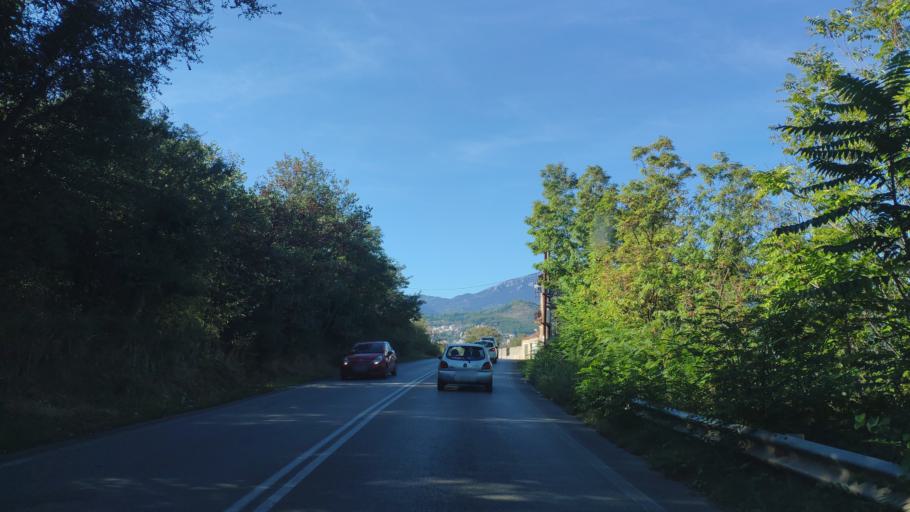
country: GR
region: Central Greece
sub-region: Nomos Voiotias
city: Livadeia
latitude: 38.4474
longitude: 22.8811
